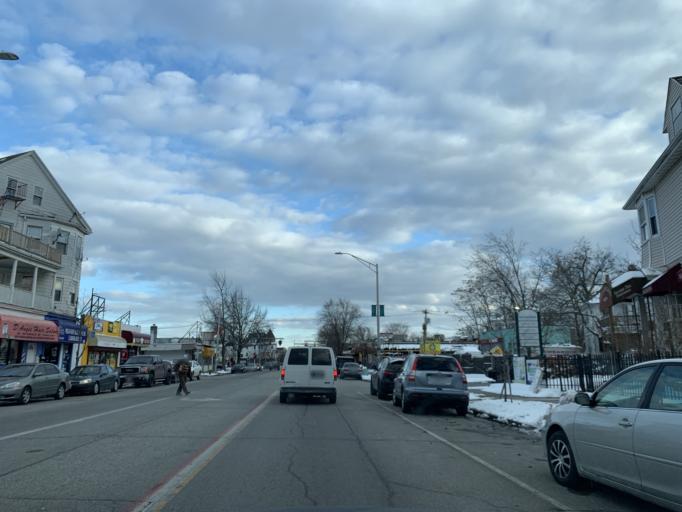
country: US
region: Rhode Island
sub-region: Providence County
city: Providence
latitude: 41.7997
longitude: -71.4166
